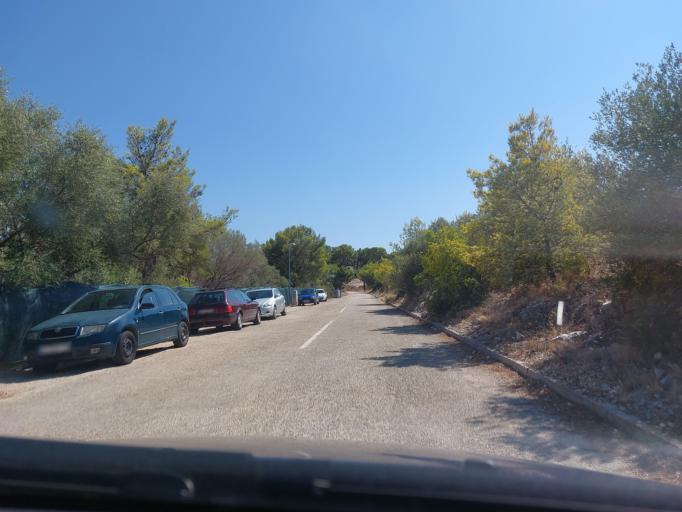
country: HR
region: Dubrovacko-Neretvanska
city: Smokvica
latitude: 42.7338
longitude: 16.8849
